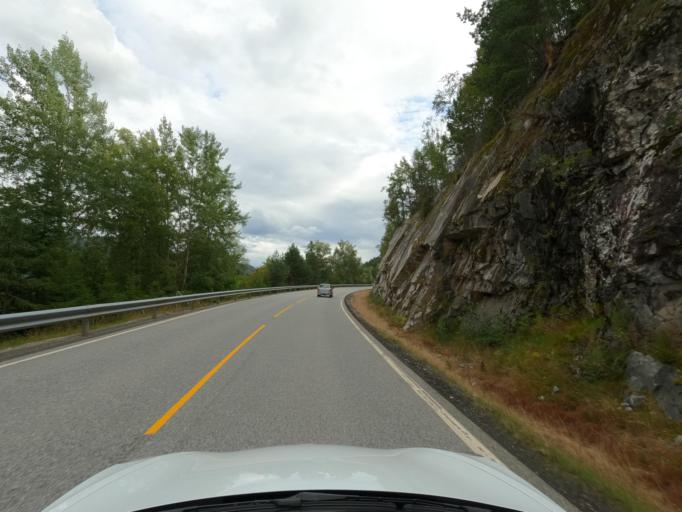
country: NO
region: Telemark
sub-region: Hjartdal
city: Sauland
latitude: 59.8055
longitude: 8.9931
